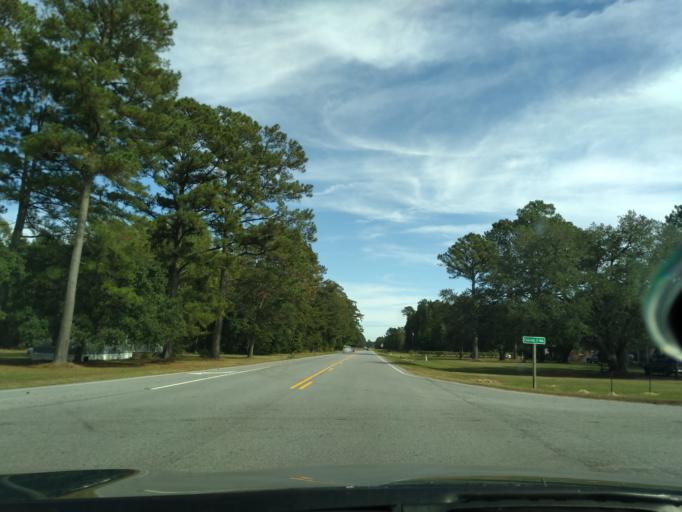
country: US
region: North Carolina
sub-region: Beaufort County
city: River Road
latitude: 35.5229
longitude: -76.8424
